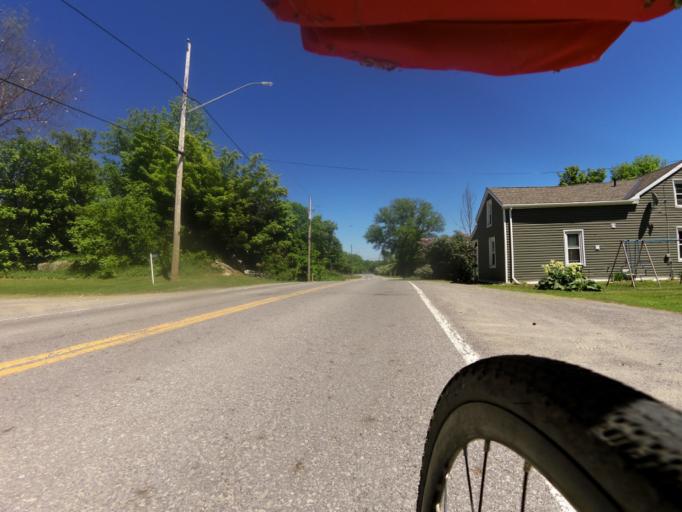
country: CA
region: Ontario
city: Carleton Place
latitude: 45.1908
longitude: -76.3302
